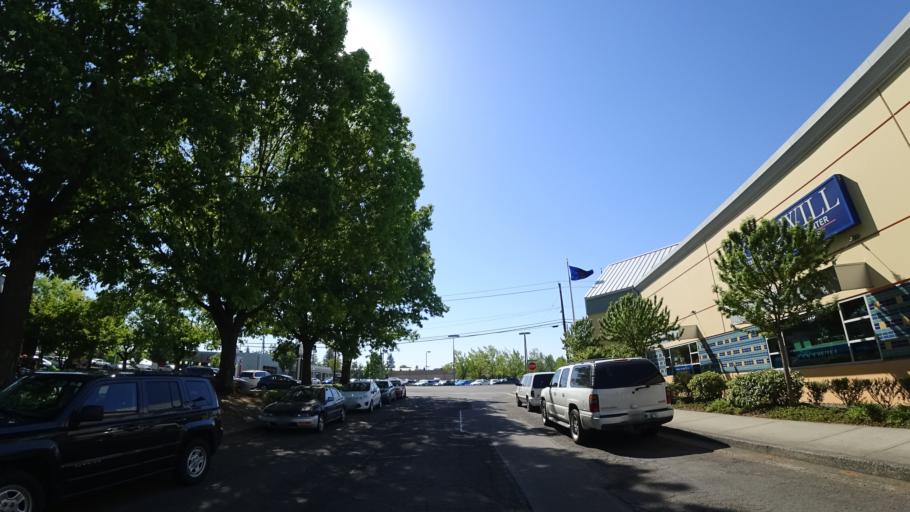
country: US
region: Oregon
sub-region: Washington County
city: Beaverton
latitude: 45.4923
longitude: -122.8100
